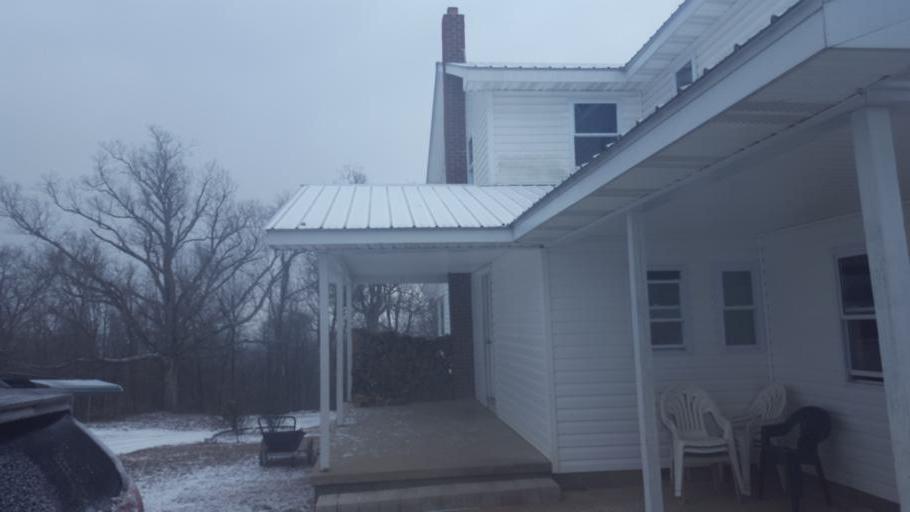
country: US
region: Kentucky
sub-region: Crittenden County
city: Marion
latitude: 37.4499
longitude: -88.0878
